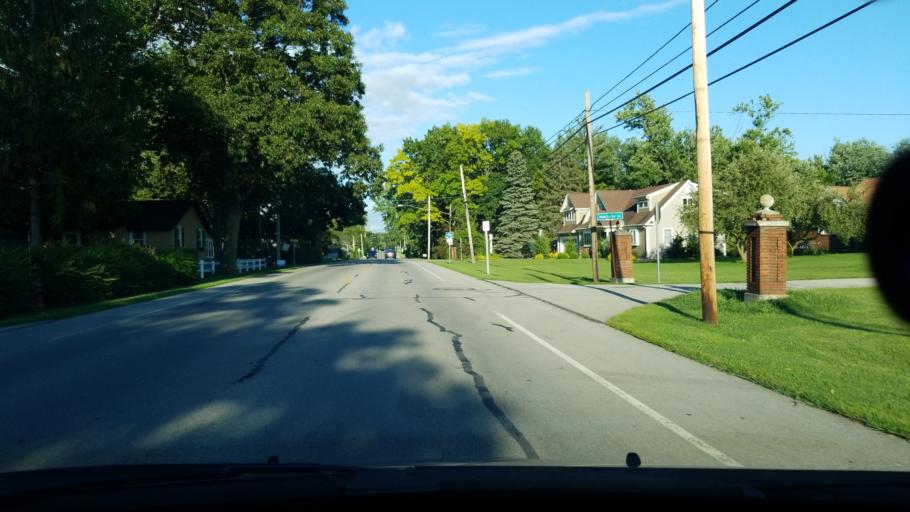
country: US
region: Ohio
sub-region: Erie County
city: Huron
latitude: 41.4081
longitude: -82.5816
